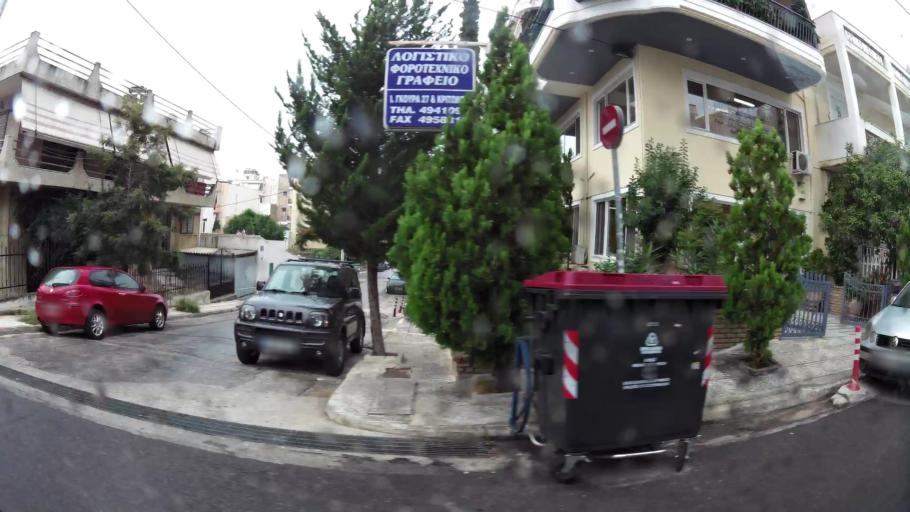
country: GR
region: Attica
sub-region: Nomos Piraios
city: Korydallos
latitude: 37.9831
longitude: 23.6364
